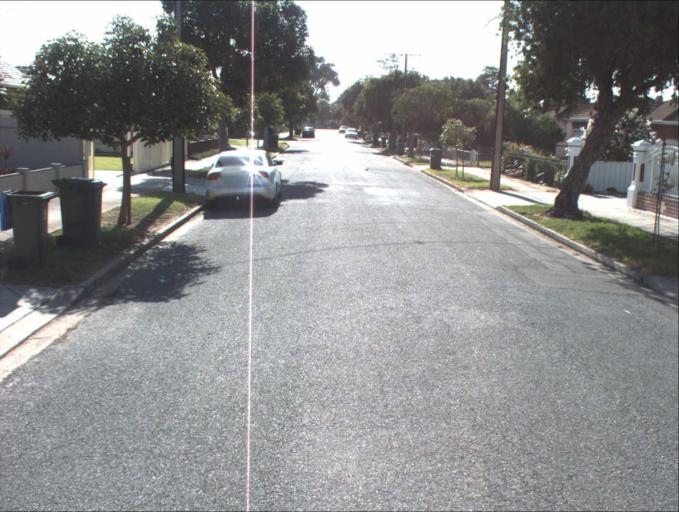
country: AU
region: South Australia
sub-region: Charles Sturt
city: Woodville
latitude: -34.8835
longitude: 138.5683
